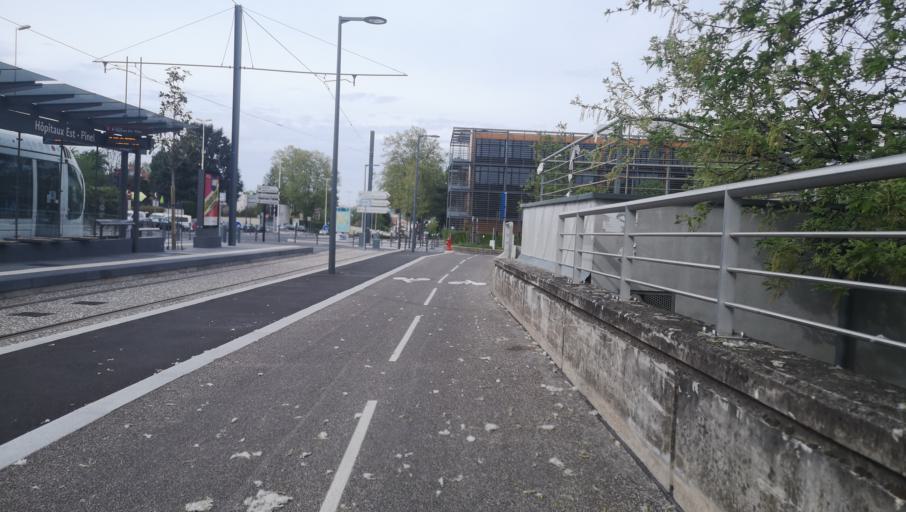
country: FR
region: Rhone-Alpes
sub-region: Departement du Rhone
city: Villeurbanne
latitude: 45.7474
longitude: 4.8969
